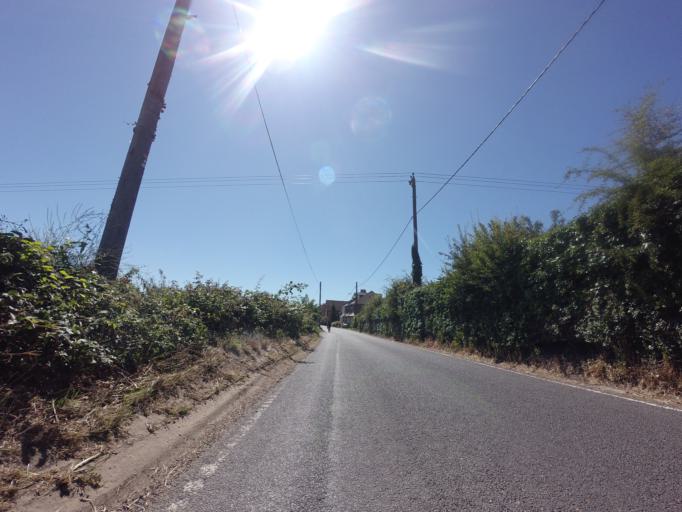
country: GB
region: England
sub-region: Kent
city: Eastry
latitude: 51.2660
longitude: 1.3042
